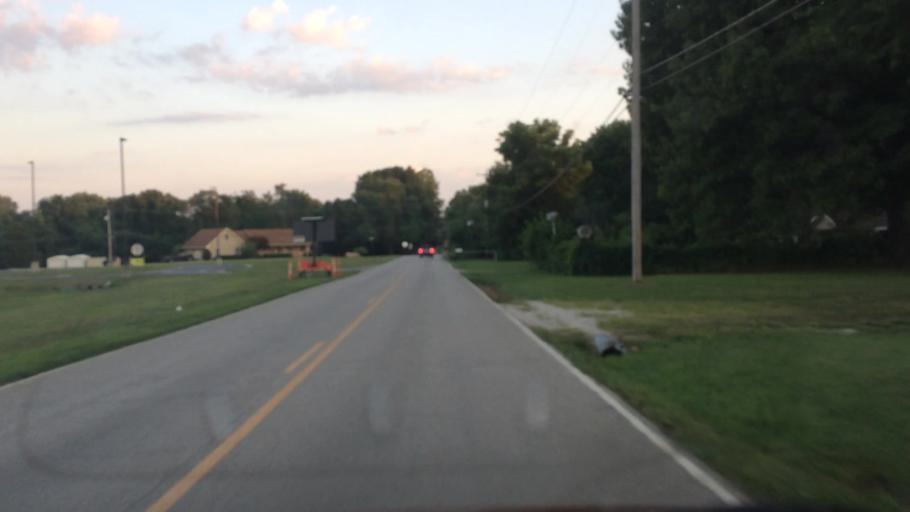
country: US
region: Missouri
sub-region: Greene County
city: Springfield
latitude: 37.1992
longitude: -93.3744
